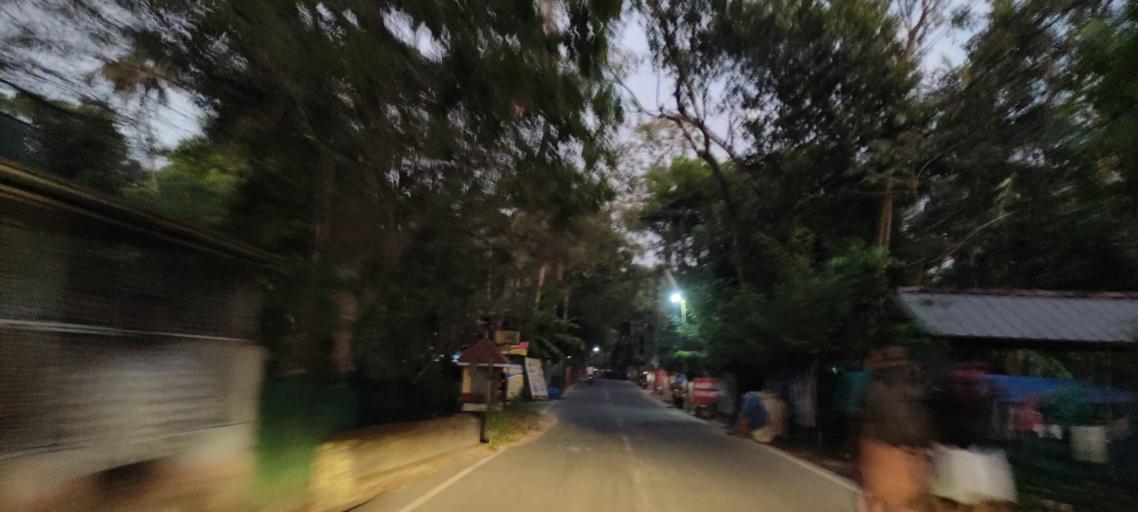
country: IN
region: Kerala
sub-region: Alappuzha
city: Kutiatodu
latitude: 9.7741
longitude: 76.3646
